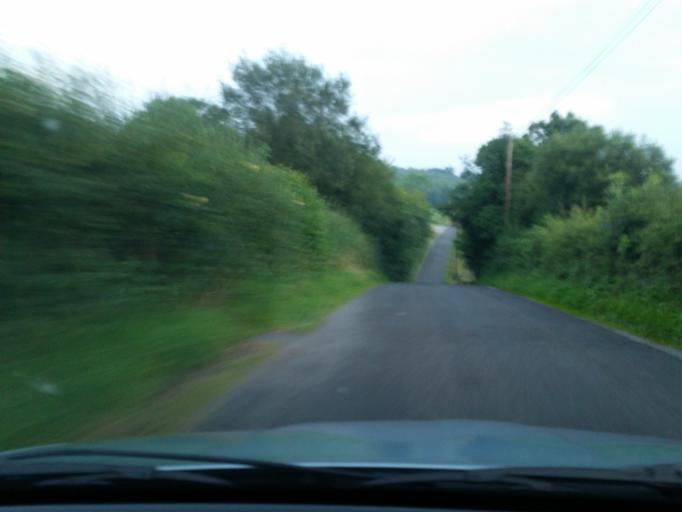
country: GB
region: Northern Ireland
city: Fivemiletown
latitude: 54.3251
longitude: -7.2958
